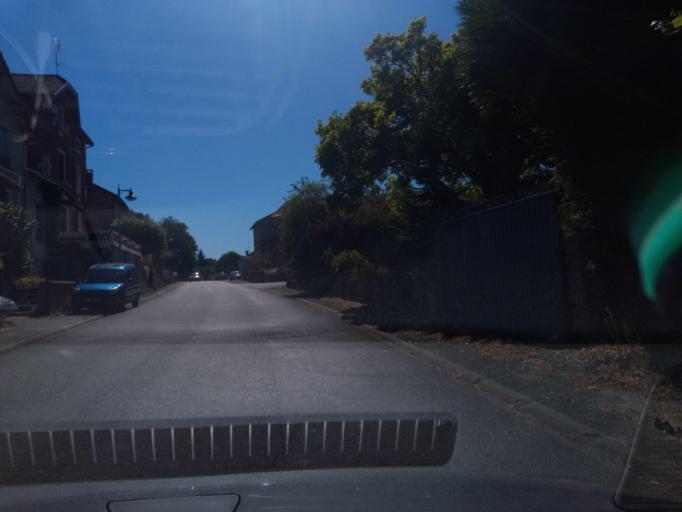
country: FR
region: Limousin
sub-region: Departement de la Haute-Vienne
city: Nantiat
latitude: 46.0753
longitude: 1.2017
